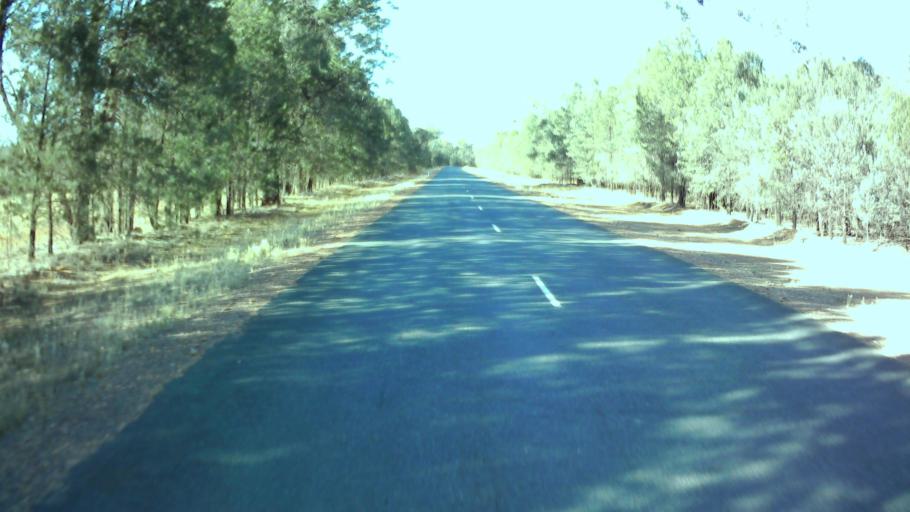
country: AU
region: New South Wales
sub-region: Weddin
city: Grenfell
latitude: -34.0270
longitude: 148.0963
